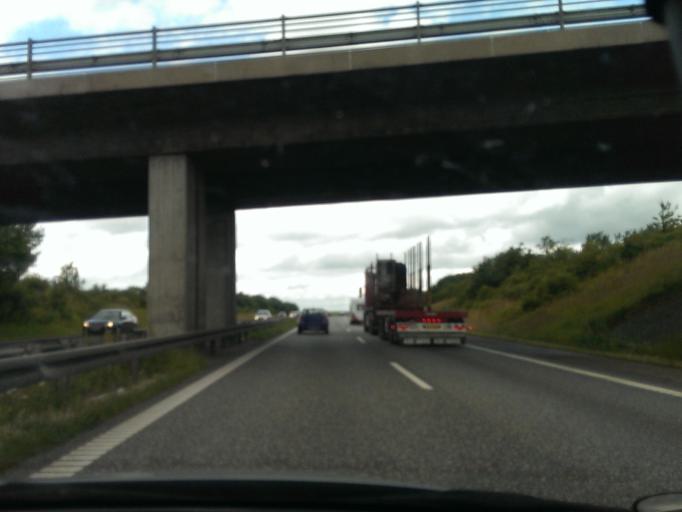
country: DK
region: North Denmark
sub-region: Mariagerfjord Kommune
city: Hobro
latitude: 56.5900
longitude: 9.7723
